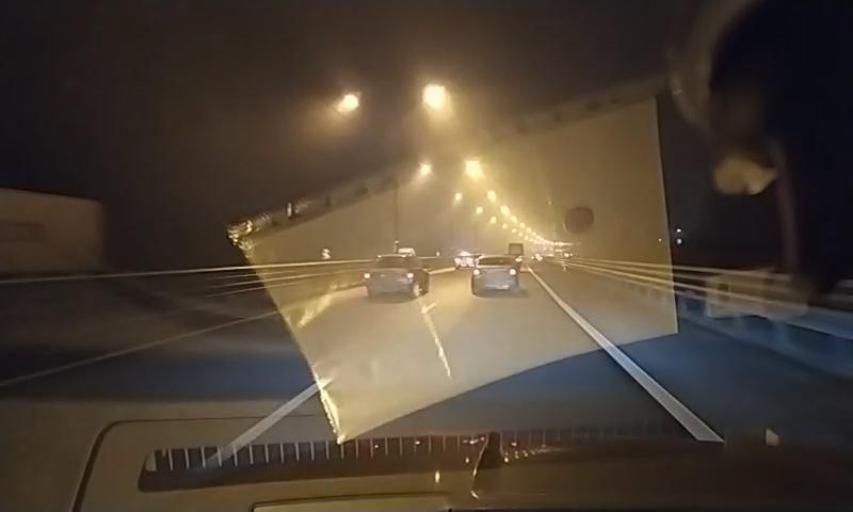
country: RU
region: Leningrad
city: Bugry
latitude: 60.1209
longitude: 30.3851
